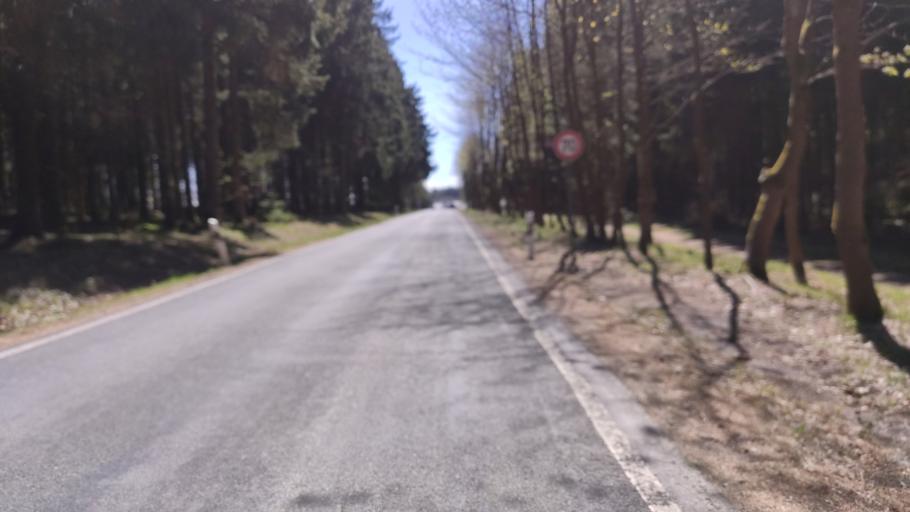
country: DE
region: Bavaria
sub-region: Upper Franconia
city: Tschirn
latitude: 50.4409
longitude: 11.4658
